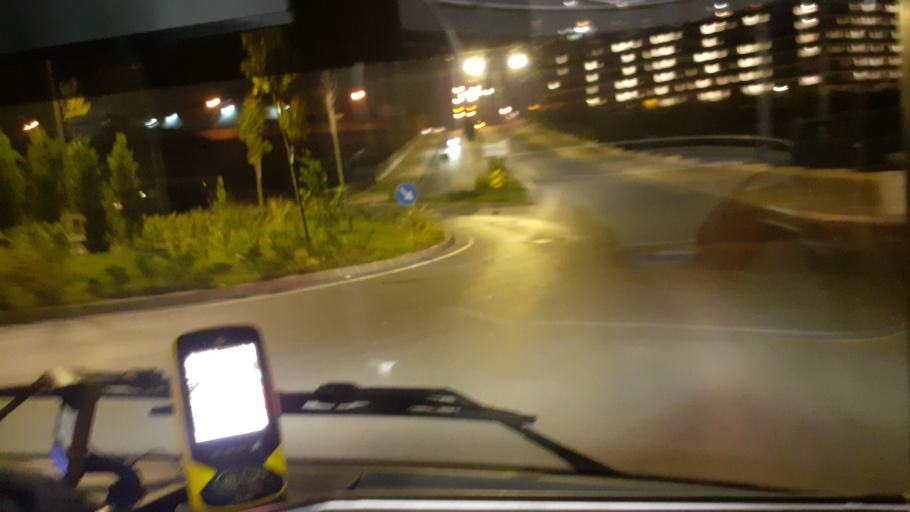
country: TR
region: Istanbul
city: Basaksehir
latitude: 41.0692
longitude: 28.7792
